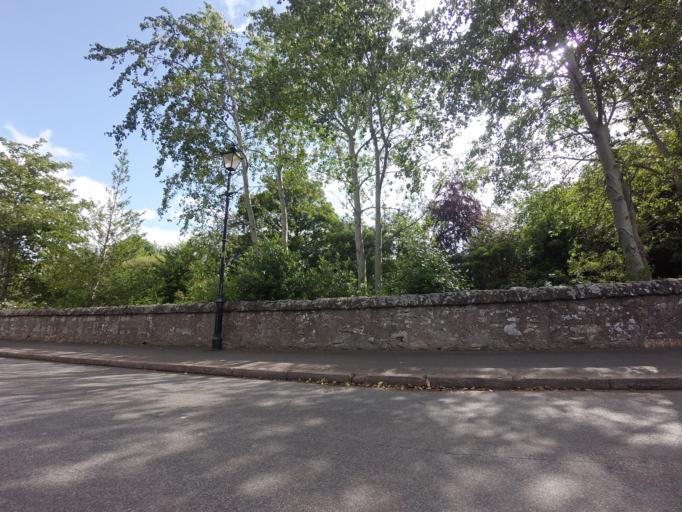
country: GB
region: Scotland
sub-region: Highland
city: Nairn
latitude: 57.5804
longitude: -3.8716
